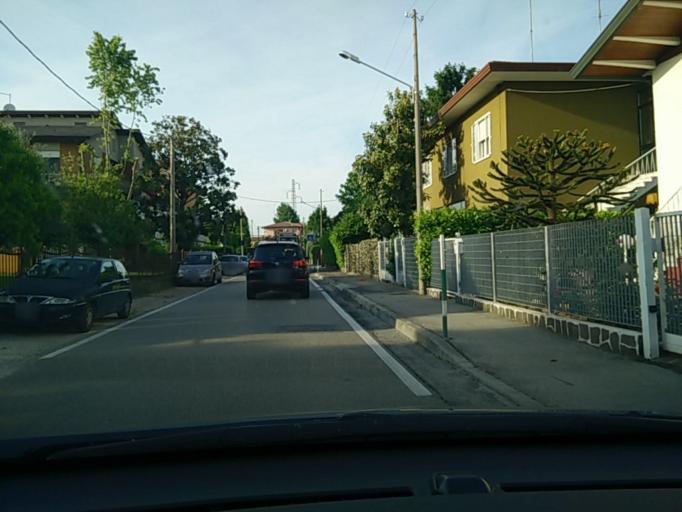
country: IT
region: Veneto
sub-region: Provincia di Padova
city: Caselle
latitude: 45.4167
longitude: 11.8349
